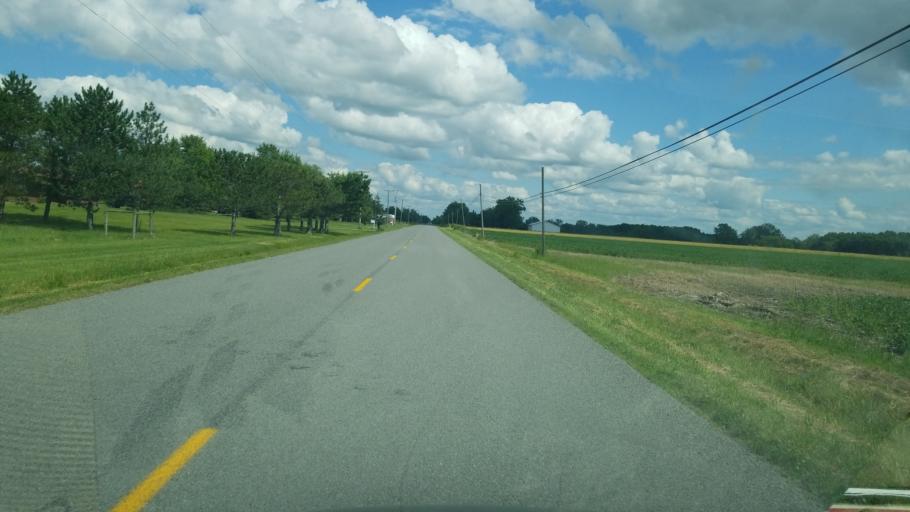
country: US
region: Ohio
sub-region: Allen County
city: Lima
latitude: 40.8318
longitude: -84.1080
